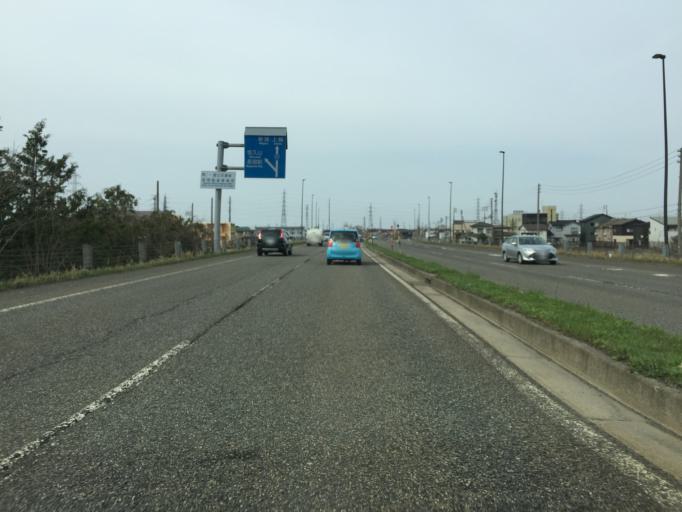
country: JP
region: Niigata
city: Nagaoka
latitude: 37.4367
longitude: 138.8675
